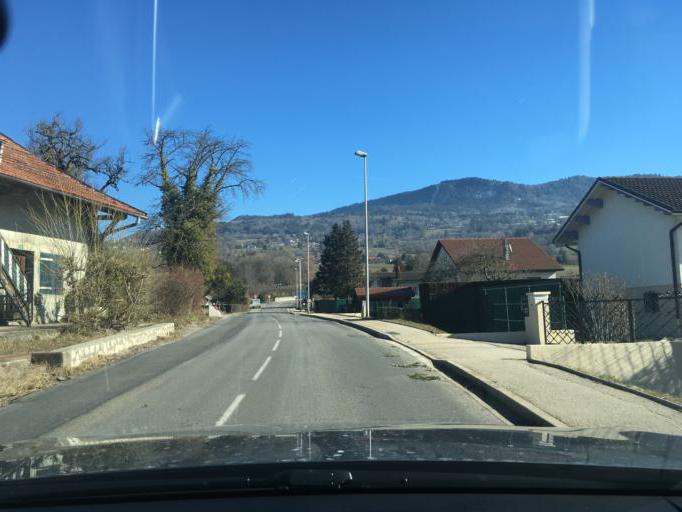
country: FR
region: Rhone-Alpes
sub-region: Departement de la Haute-Savoie
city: Cranves-Sales
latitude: 46.1806
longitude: 6.3030
